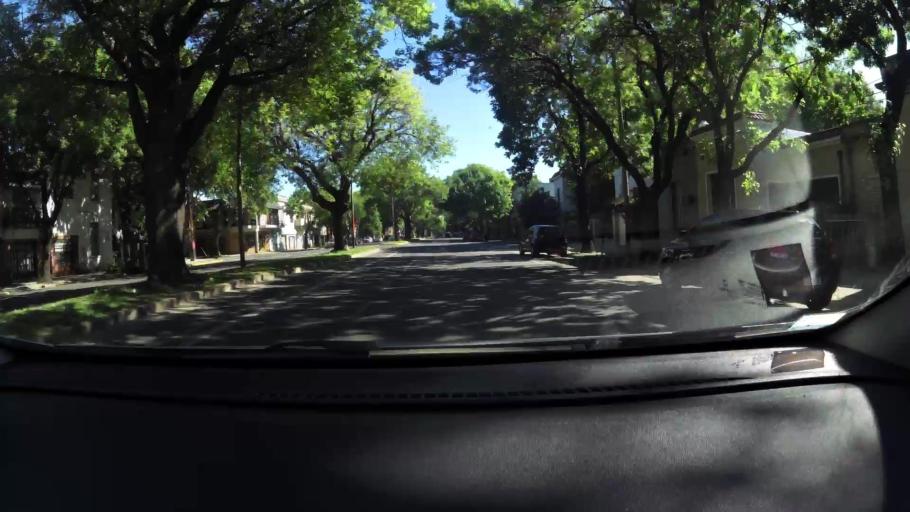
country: AR
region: Santa Fe
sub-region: Departamento de Rosario
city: Rosario
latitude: -32.9608
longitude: -60.6703
